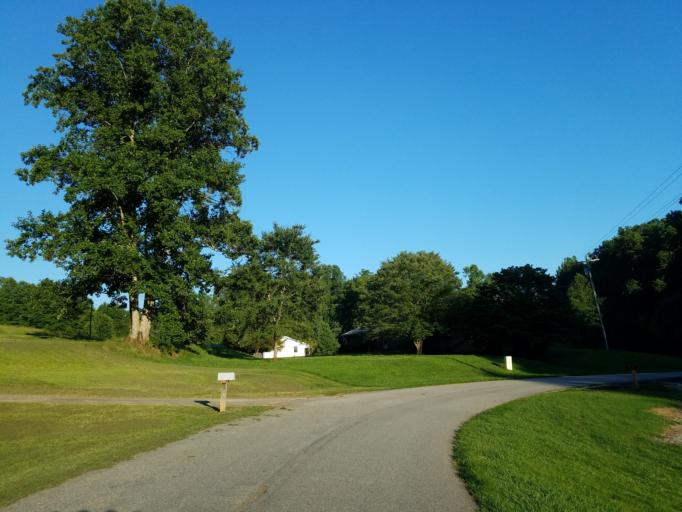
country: US
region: Georgia
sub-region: Lumpkin County
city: Dahlonega
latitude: 34.5734
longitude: -83.9741
